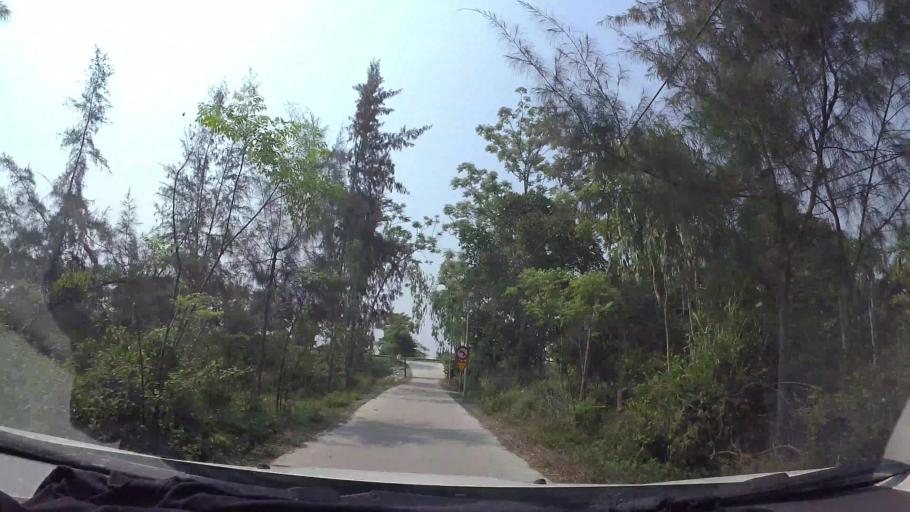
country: VN
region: Da Nang
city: Cam Le
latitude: 15.9741
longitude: 108.2265
